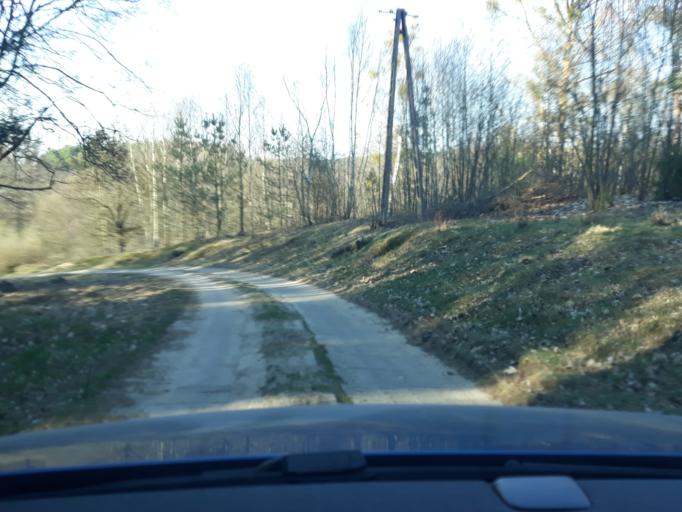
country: PL
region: Pomeranian Voivodeship
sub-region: Powiat bytowski
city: Lipnica
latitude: 53.9240
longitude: 17.4469
